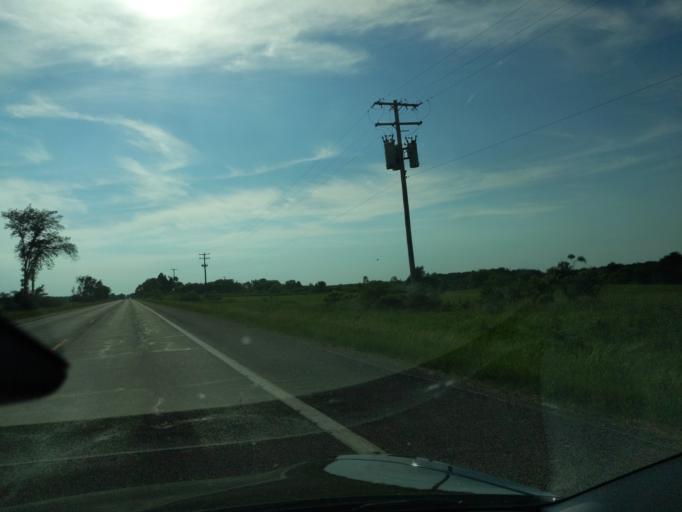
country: US
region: Michigan
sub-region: Barry County
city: Nashville
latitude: 42.6035
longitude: -85.1387
